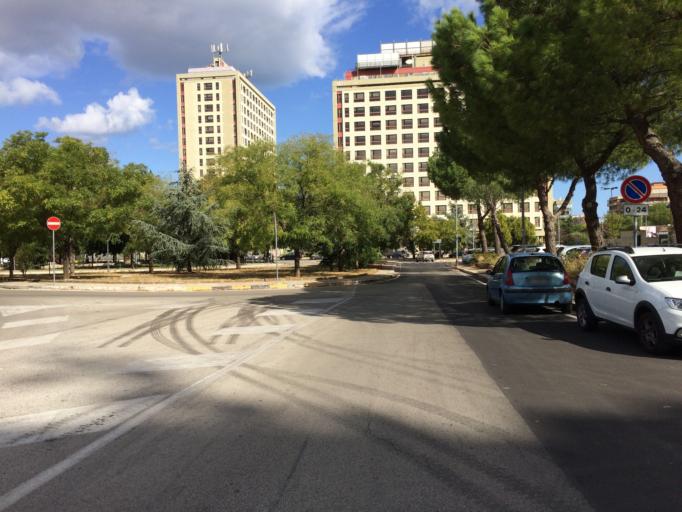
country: IT
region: Apulia
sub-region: Provincia di Bari
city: Bari
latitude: 41.0953
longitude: 16.8620
